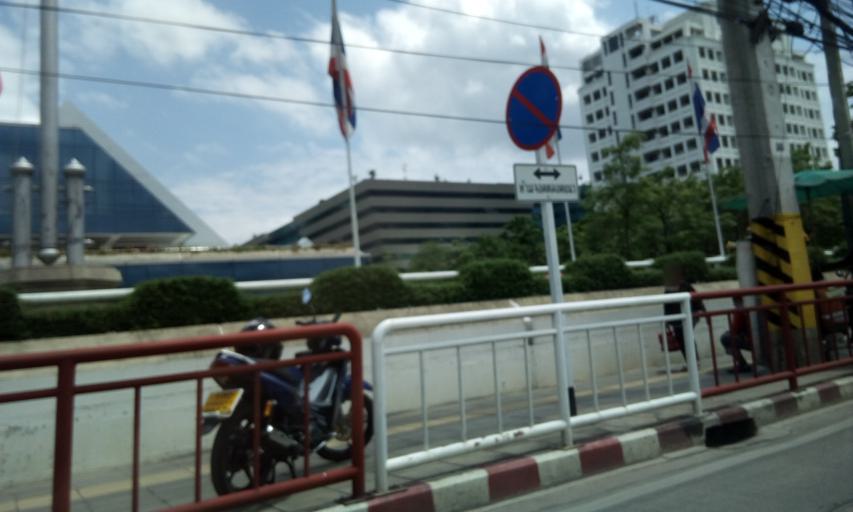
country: TH
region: Bangkok
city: Lak Si
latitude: 13.8906
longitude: 100.5670
